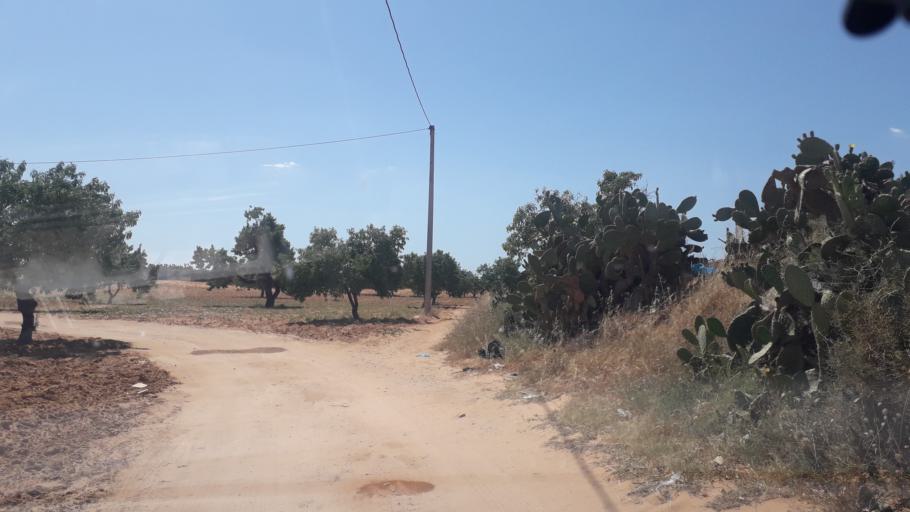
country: TN
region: Safaqis
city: Al Qarmadah
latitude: 34.8298
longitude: 10.7691
